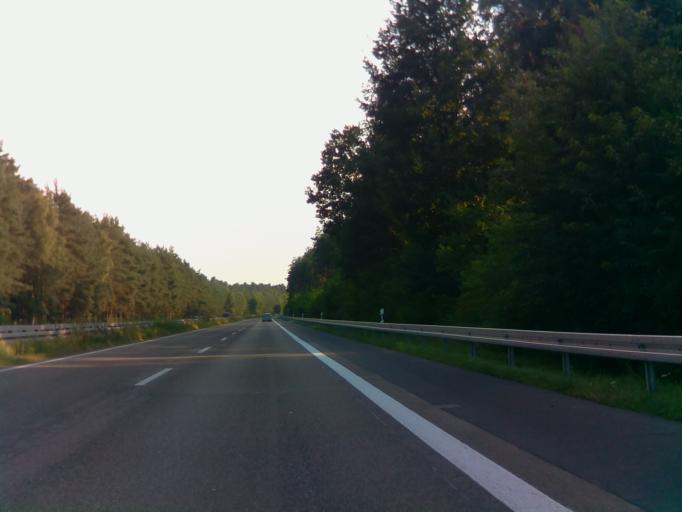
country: DE
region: Hesse
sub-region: Regierungsbezirk Darmstadt
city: Eppertshausen
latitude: 49.9736
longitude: 8.8640
